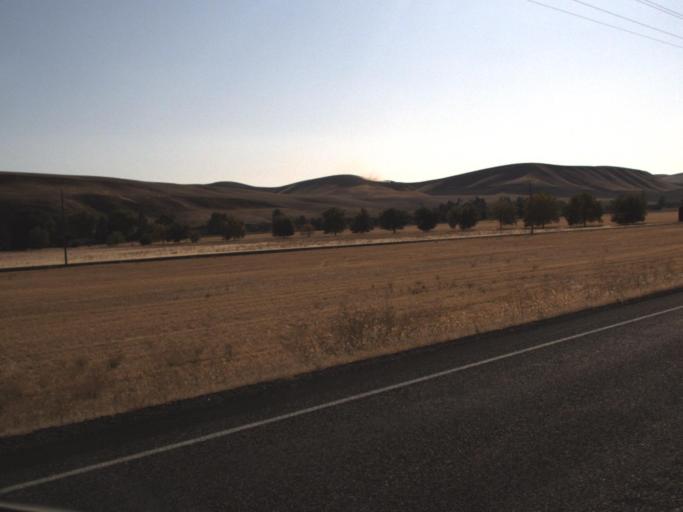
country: US
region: Washington
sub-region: Walla Walla County
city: Garrett
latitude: 46.2970
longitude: -118.4408
